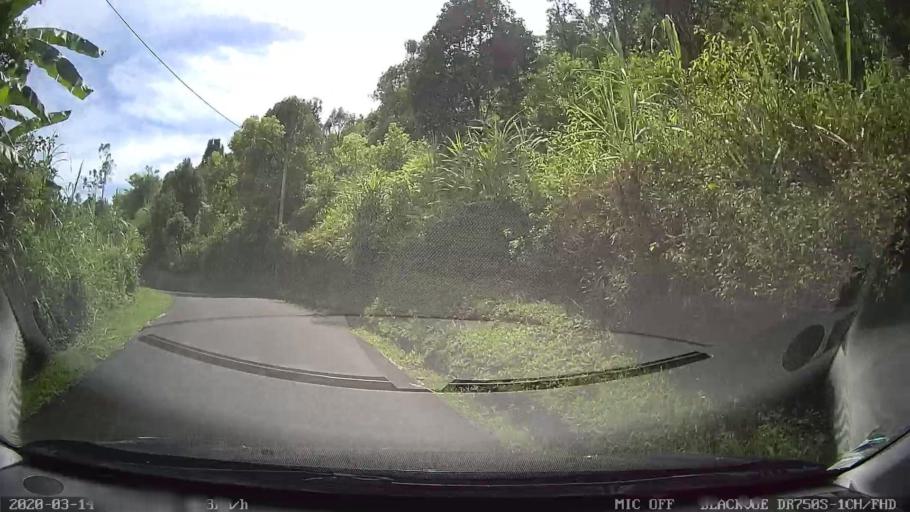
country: RE
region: Reunion
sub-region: Reunion
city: Sainte-Marie
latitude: -20.9485
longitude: 55.5266
